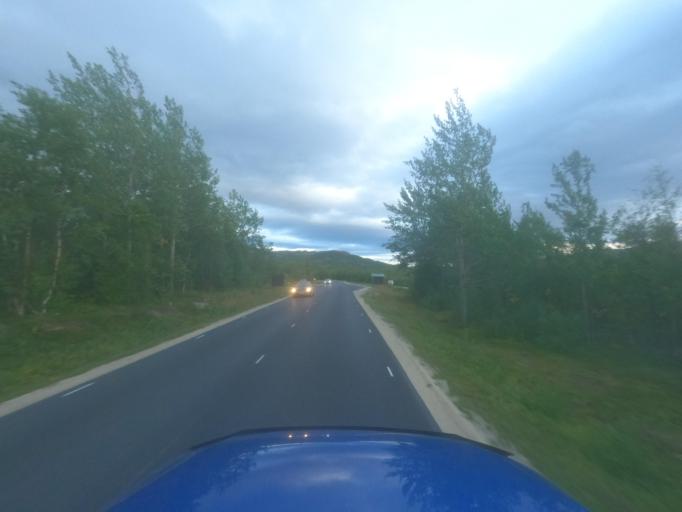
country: NO
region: Finnmark Fylke
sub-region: Porsanger
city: Lakselv
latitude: 69.9760
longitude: 24.9644
